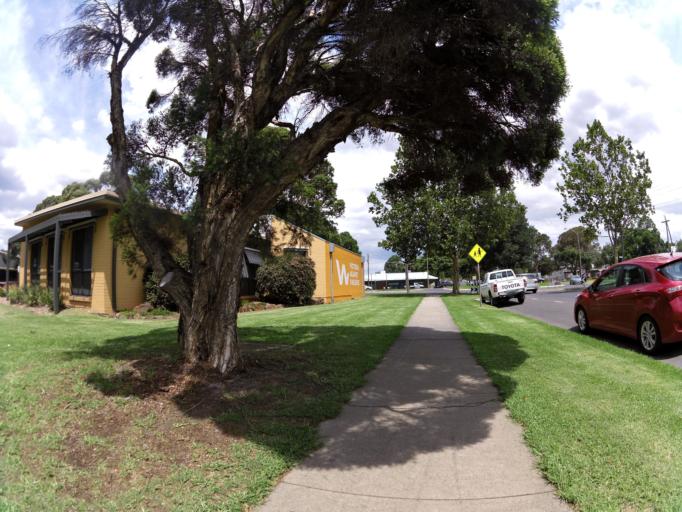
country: AU
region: Victoria
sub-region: Latrobe
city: Traralgon
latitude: -38.1935
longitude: 146.5337
